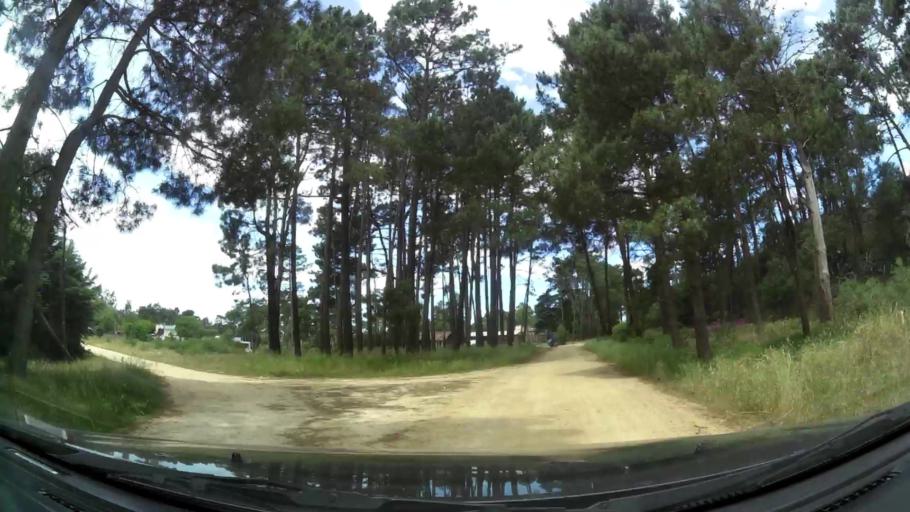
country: UY
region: Canelones
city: Empalme Olmos
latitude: -34.7951
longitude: -55.8927
